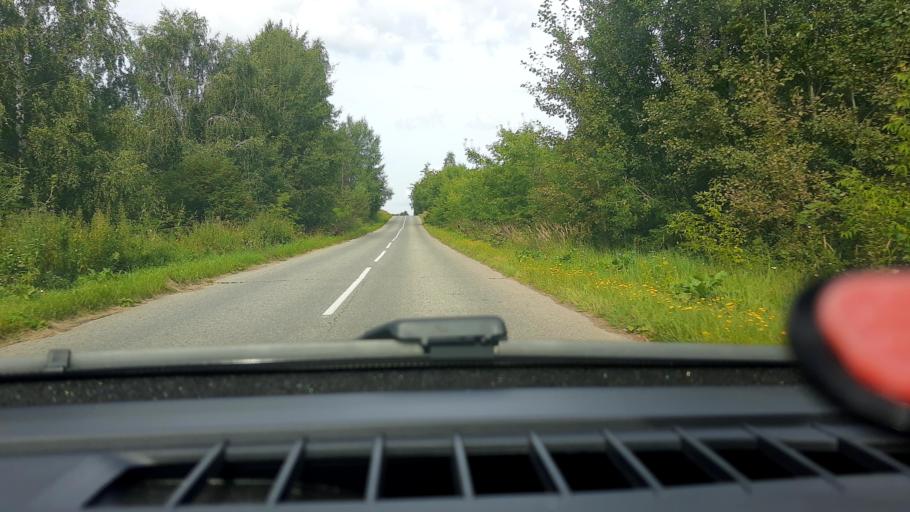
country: RU
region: Nizjnij Novgorod
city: Burevestnik
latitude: 56.0471
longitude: 43.7076
